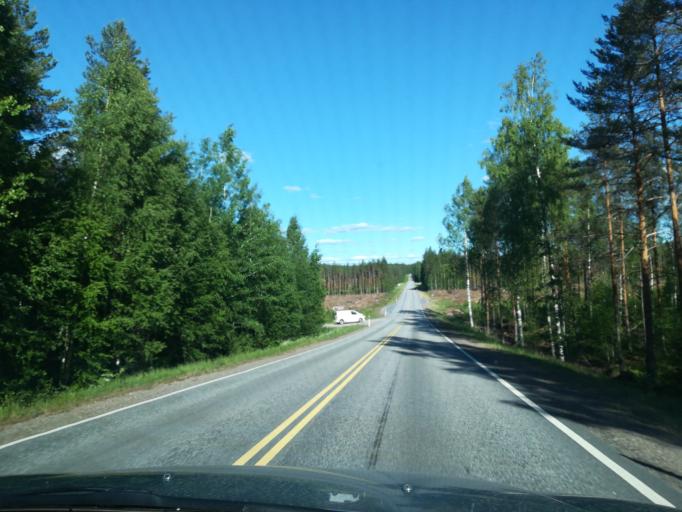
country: FI
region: South Karelia
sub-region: Imatra
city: Ruokolahti
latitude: 61.4039
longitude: 28.5756
